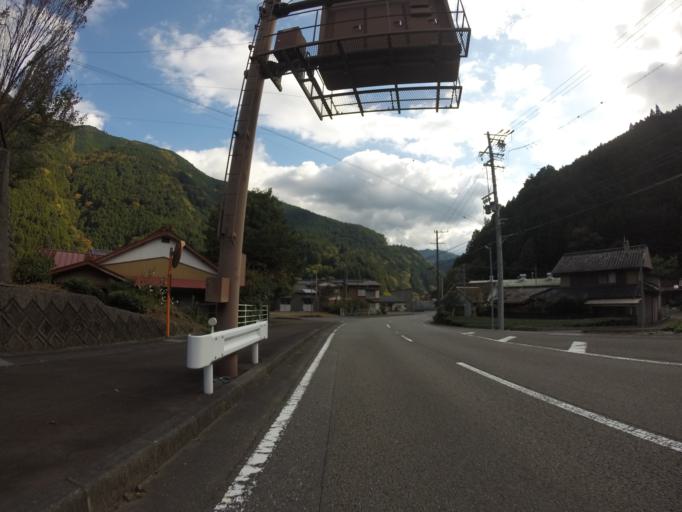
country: JP
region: Shizuoka
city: Shizuoka-shi
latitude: 35.1520
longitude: 138.1457
